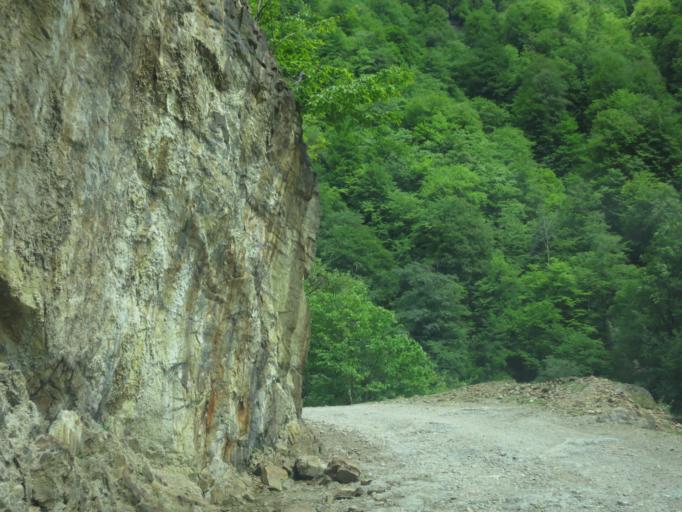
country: GE
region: Kakheti
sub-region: Telavi
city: Telavi
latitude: 42.2191
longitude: 45.4778
